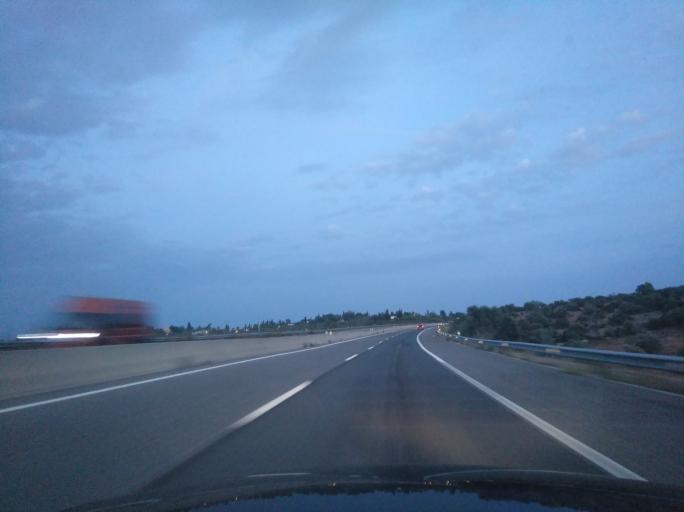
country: PT
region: Faro
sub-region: Portimao
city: Alvor
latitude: 37.1834
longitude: -8.5942
